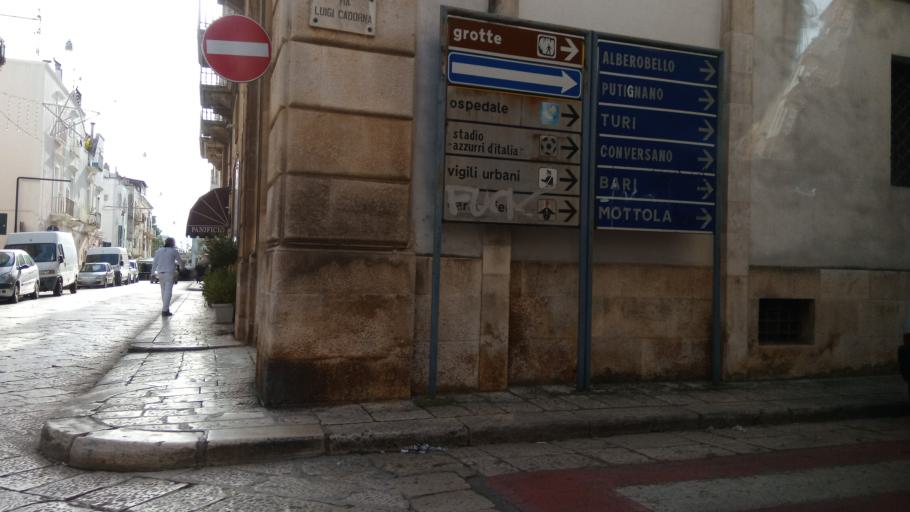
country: IT
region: Apulia
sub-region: Provincia di Bari
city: Castellana
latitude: 40.8863
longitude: 17.1669
